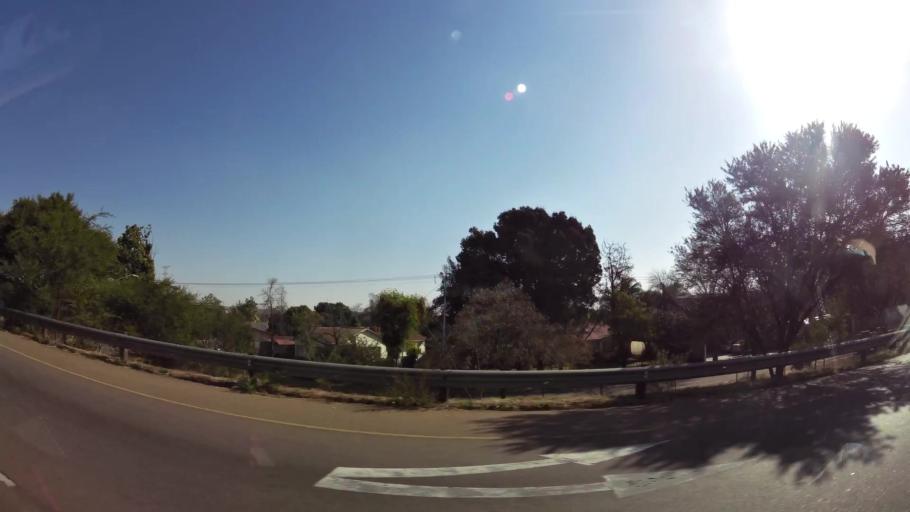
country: ZA
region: Gauteng
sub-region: City of Tshwane Metropolitan Municipality
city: Pretoria
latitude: -25.7218
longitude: 28.2580
